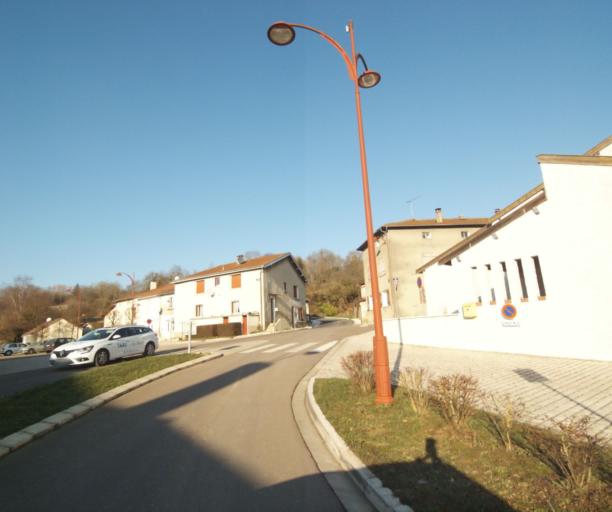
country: FR
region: Champagne-Ardenne
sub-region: Departement de la Haute-Marne
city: Chevillon
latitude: 48.5440
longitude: 5.1019
